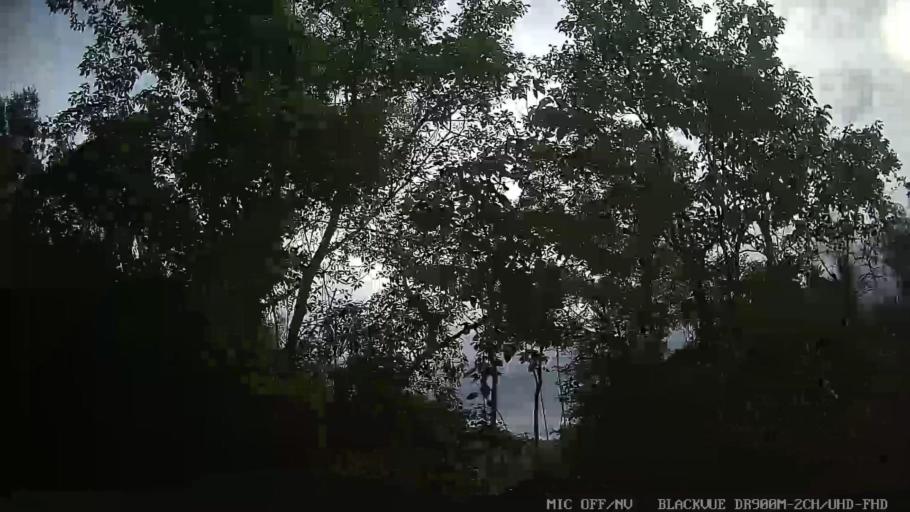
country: BR
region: Sao Paulo
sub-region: Amparo
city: Amparo
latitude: -22.7660
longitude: -46.7601
